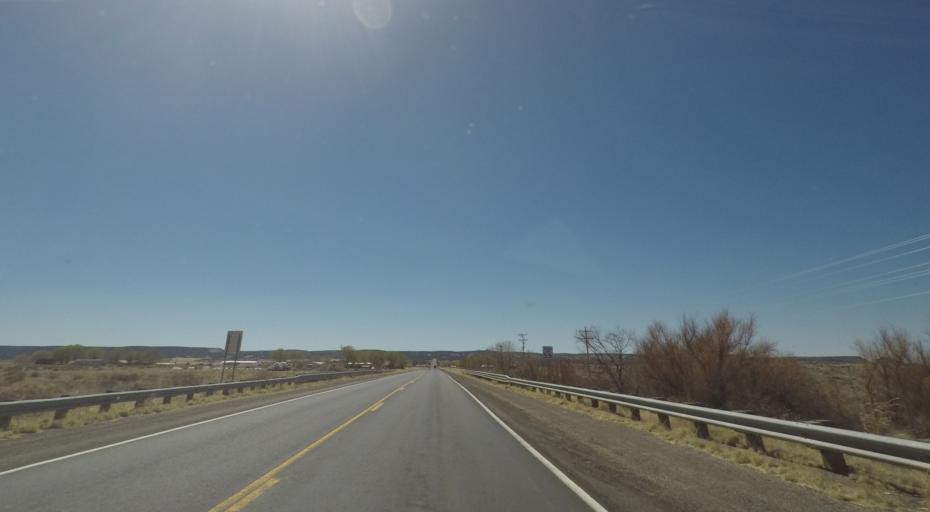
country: US
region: New Mexico
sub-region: Catron County
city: Reserve
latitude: 34.3440
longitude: -108.5060
